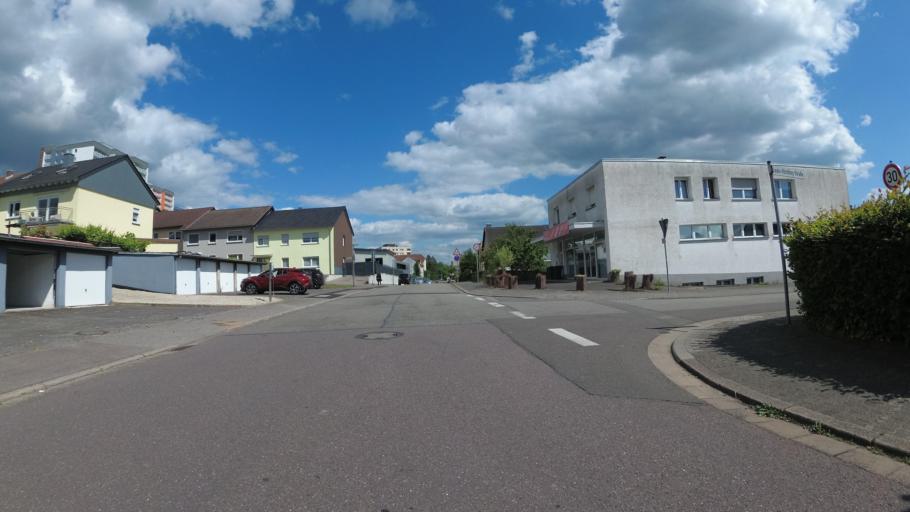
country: DE
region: Saarland
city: Volklingen
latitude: 49.2596
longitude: 6.8486
